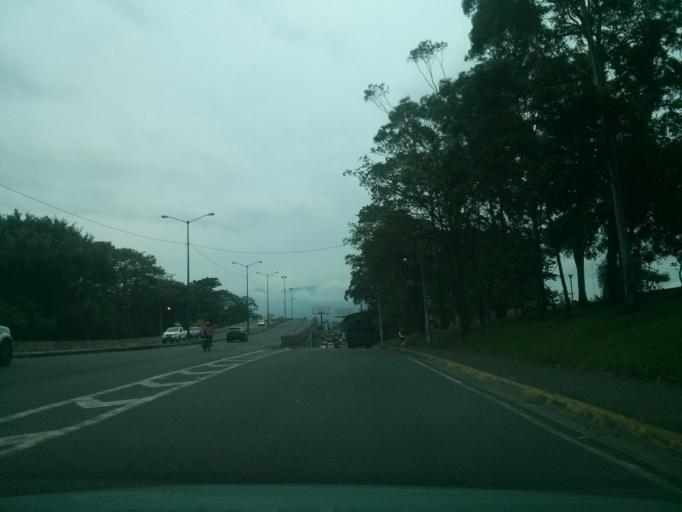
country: CR
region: San Jose
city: San Jose
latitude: 9.9143
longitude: -84.0714
